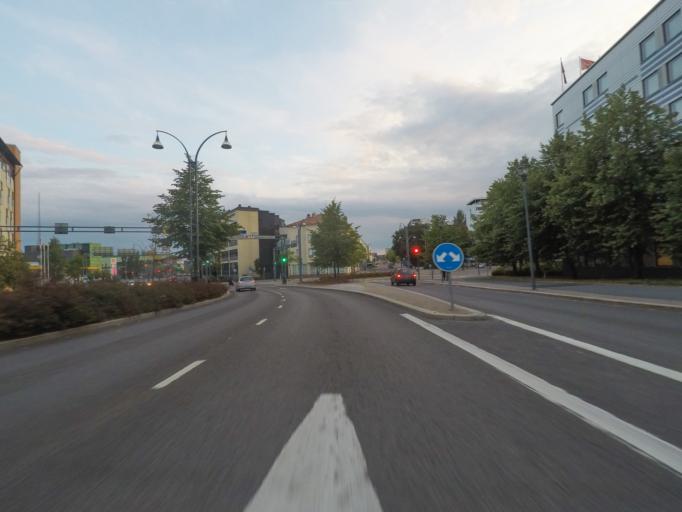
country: FI
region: Central Finland
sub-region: Jyvaeskylae
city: Jyvaeskylae
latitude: 62.2448
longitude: 25.7557
